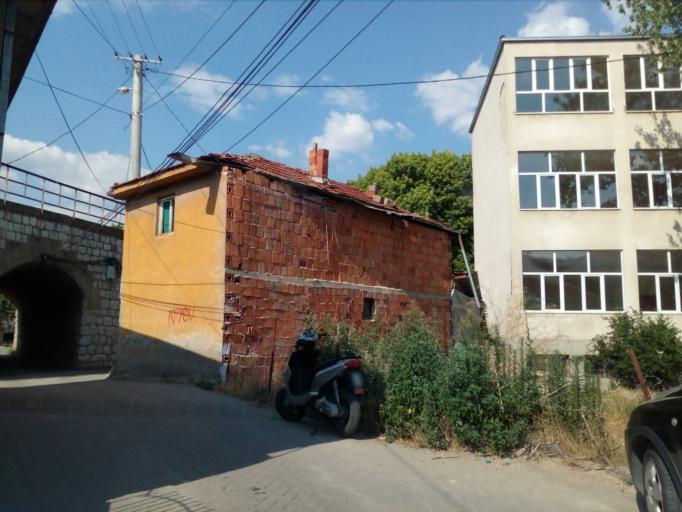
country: MK
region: Veles
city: Veles
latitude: 41.7183
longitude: 21.7849
